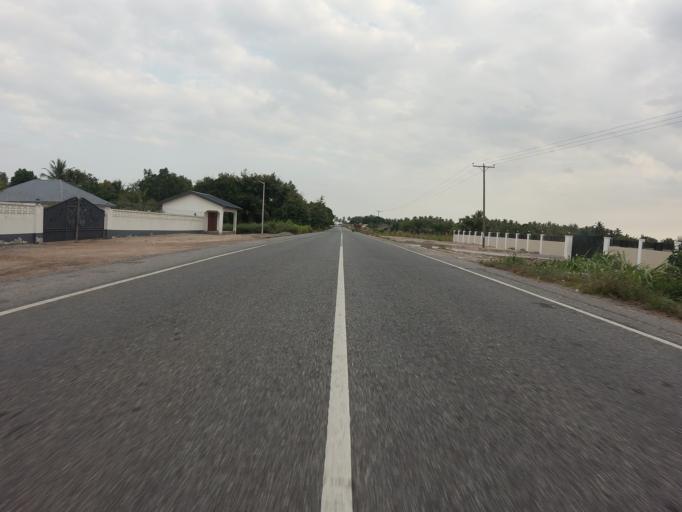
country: GH
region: Volta
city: Ho
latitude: 6.2379
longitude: 0.5511
